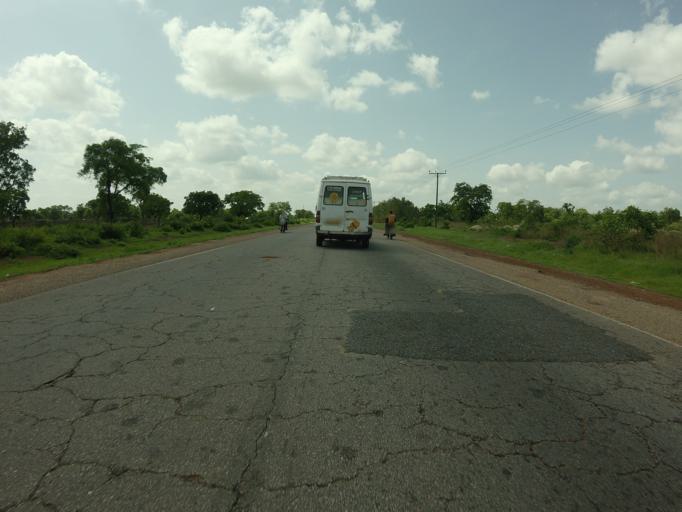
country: GH
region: Northern
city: Savelugu
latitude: 9.5904
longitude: -0.8325
